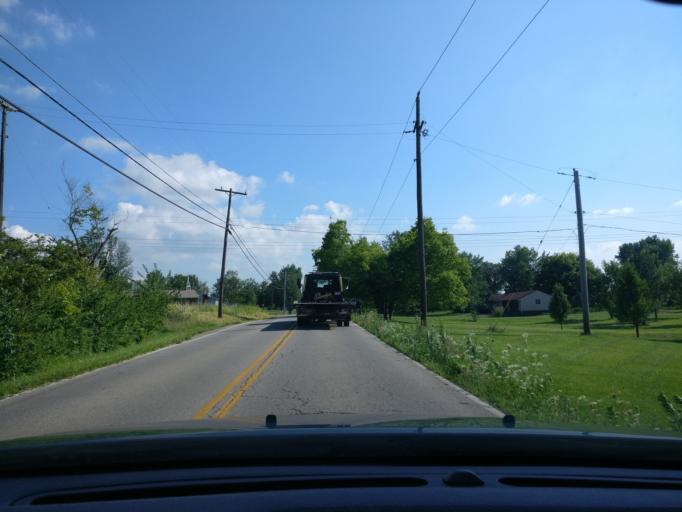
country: US
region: Ohio
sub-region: Warren County
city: Springboro
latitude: 39.5858
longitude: -84.2486
